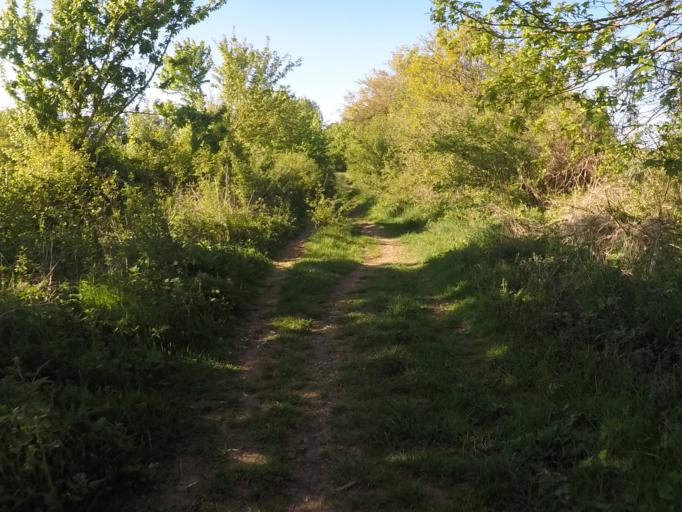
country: GB
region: England
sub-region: Oxfordshire
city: Stonesfield
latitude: 51.8762
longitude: -1.4471
